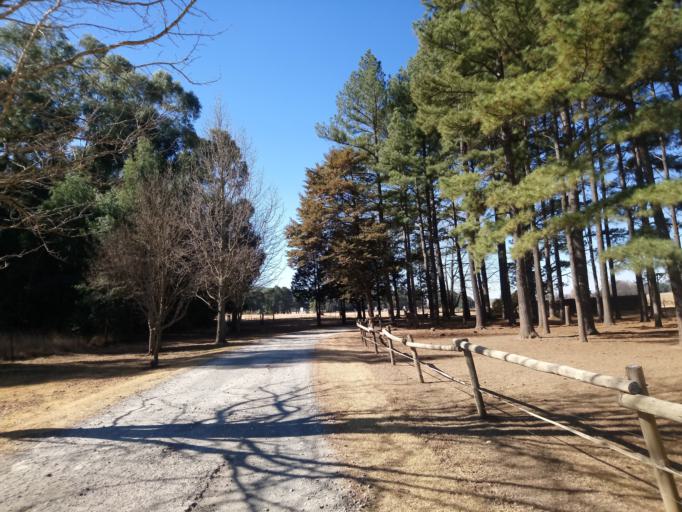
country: ZA
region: KwaZulu-Natal
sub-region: uMgungundlovu District Municipality
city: Mooirivier
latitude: -29.3229
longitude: 29.7169
